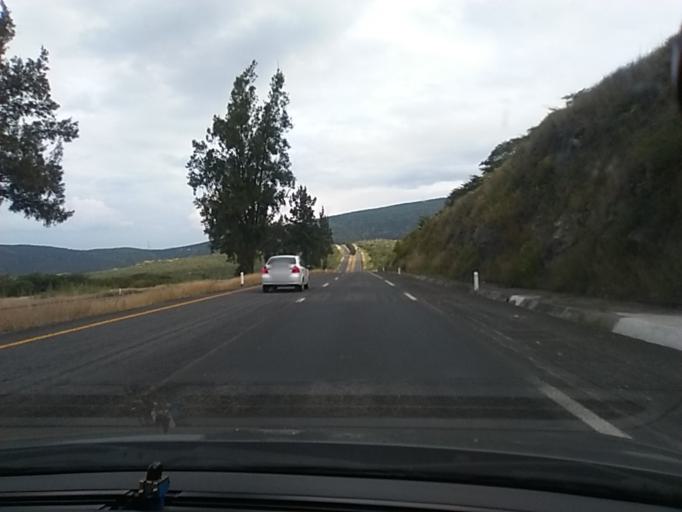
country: MX
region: Michoacan
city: Ixtlan
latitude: 20.2191
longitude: -102.3646
